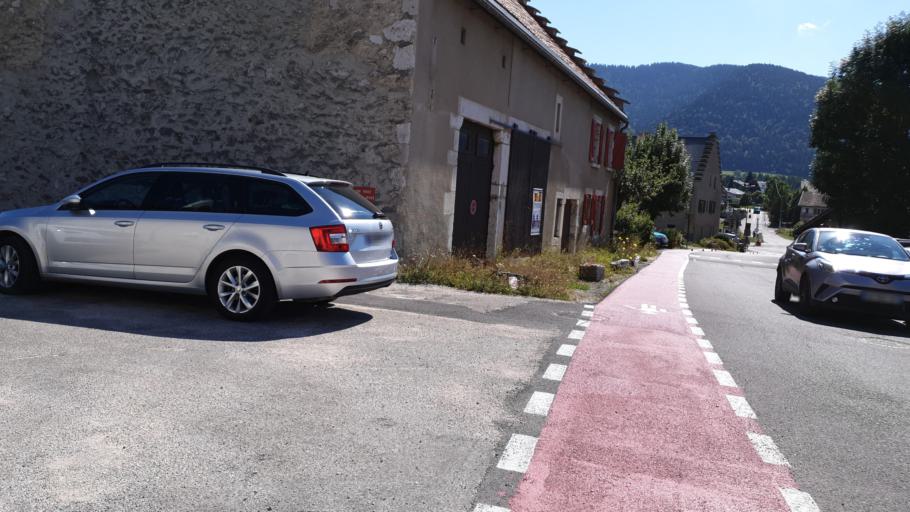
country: FR
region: Rhone-Alpes
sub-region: Departement de l'Isere
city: Autrans
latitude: 45.1769
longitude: 5.5435
